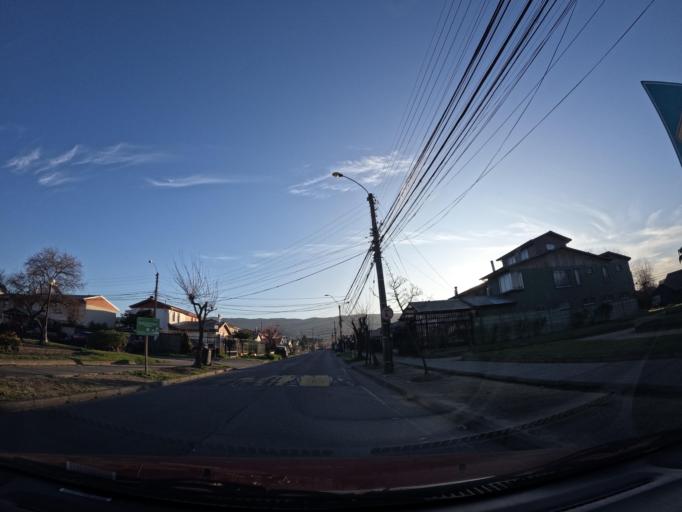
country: CL
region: Biobio
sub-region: Provincia de Concepcion
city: Chiguayante
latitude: -36.9211
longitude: -73.0321
